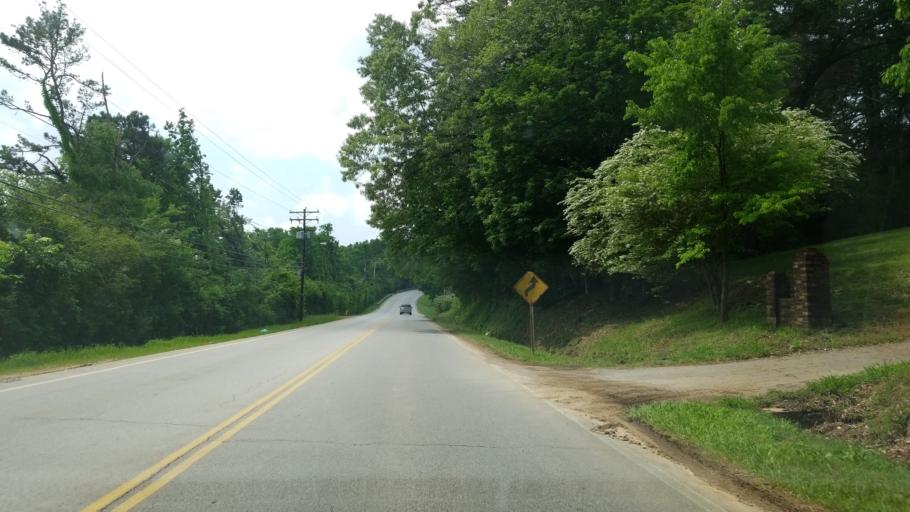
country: US
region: Tennessee
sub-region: Hamilton County
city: Falling Water
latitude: 35.2003
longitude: -85.2389
